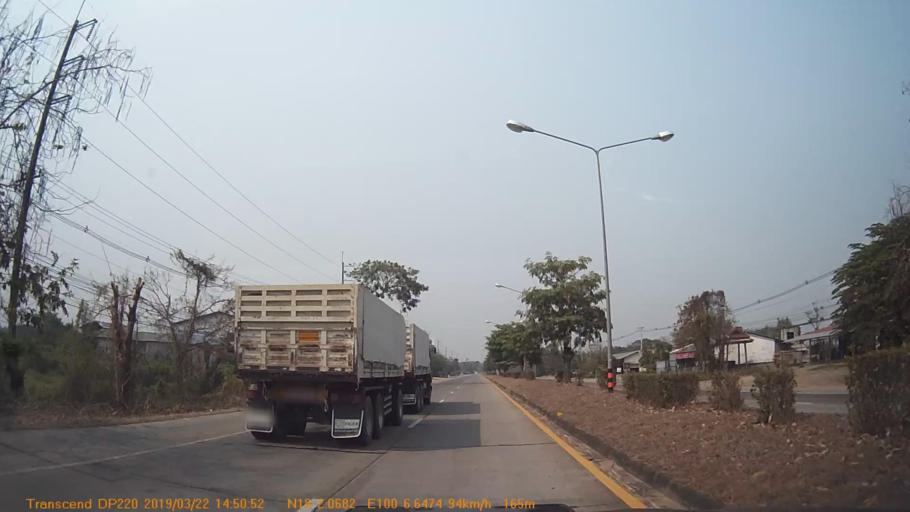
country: TH
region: Phrae
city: Sung Men
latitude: 18.0347
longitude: 100.1108
